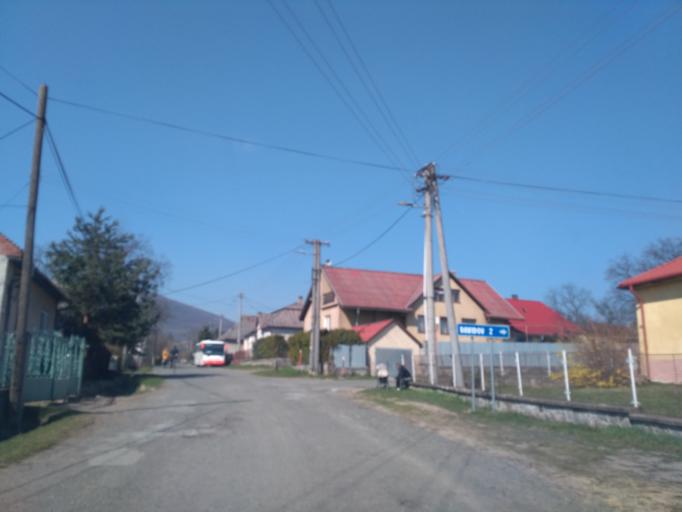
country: SK
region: Presovsky
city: Vranov nad Topl'ou
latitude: 48.8049
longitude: 21.6402
